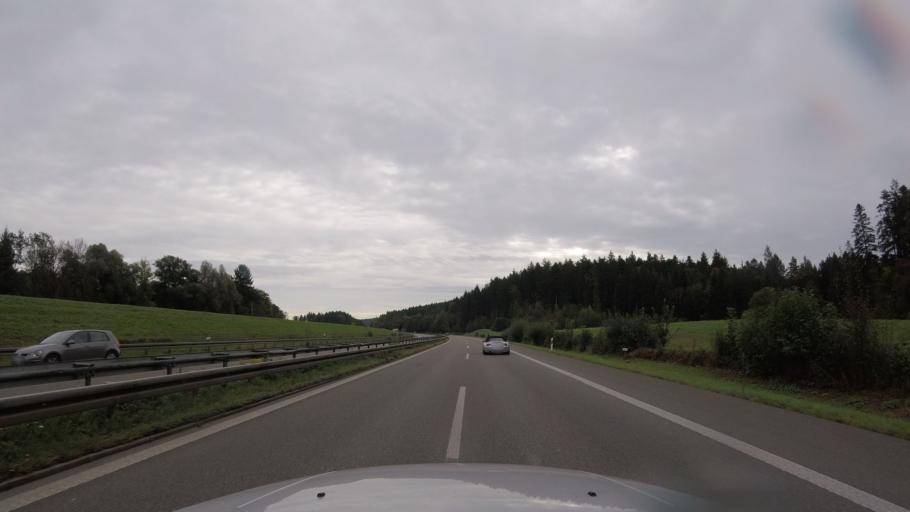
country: DE
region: Baden-Wuerttemberg
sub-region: Regierungsbezirk Stuttgart
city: Lorch
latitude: 48.7899
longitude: 9.7227
